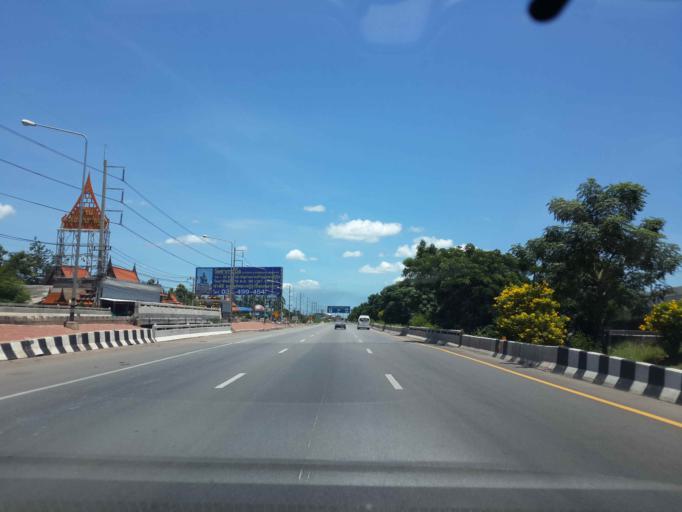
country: TH
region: Ratchaburi
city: Pak Tho
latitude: 13.3434
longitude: 99.8593
